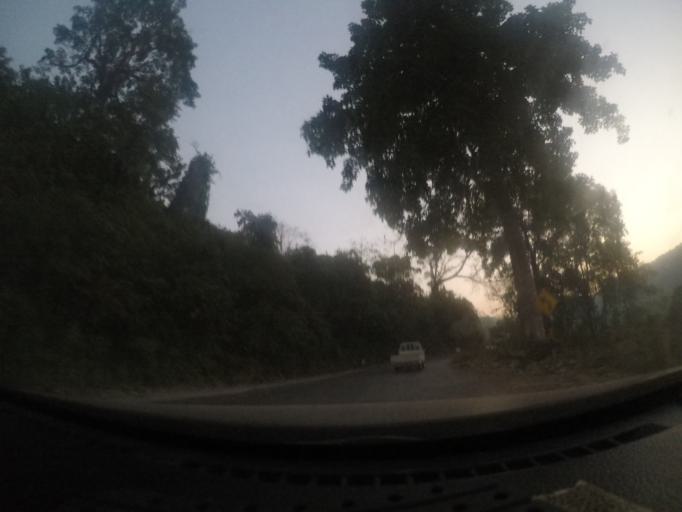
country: MM
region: Mandalay
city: Yamethin
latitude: 20.6967
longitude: 96.5068
